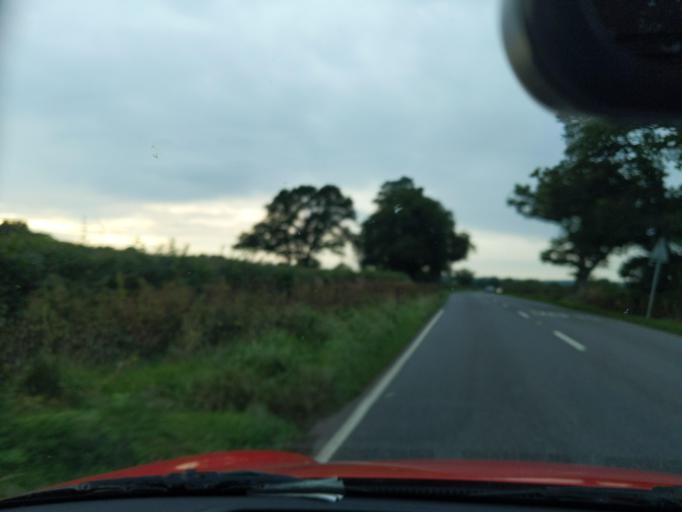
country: GB
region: England
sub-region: Devon
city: Okehampton
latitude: 50.8110
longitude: -4.0599
